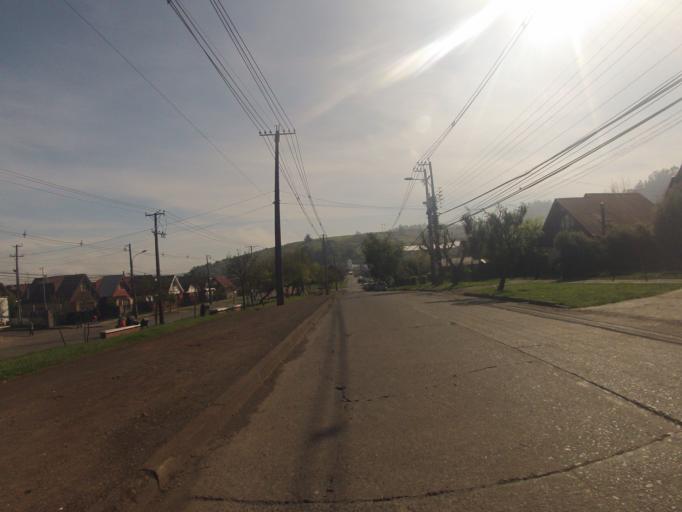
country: CL
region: Araucania
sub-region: Provincia de Cautin
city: Temuco
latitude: -38.7288
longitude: -72.5991
